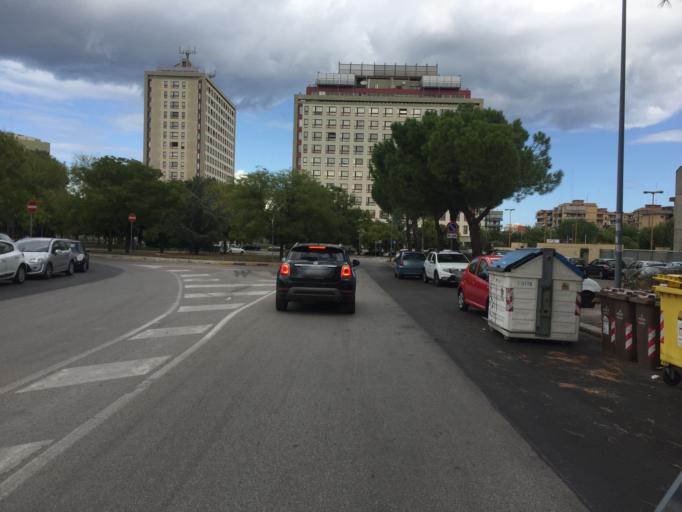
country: IT
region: Apulia
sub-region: Provincia di Bari
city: Bari
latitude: 41.0952
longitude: 16.8619
